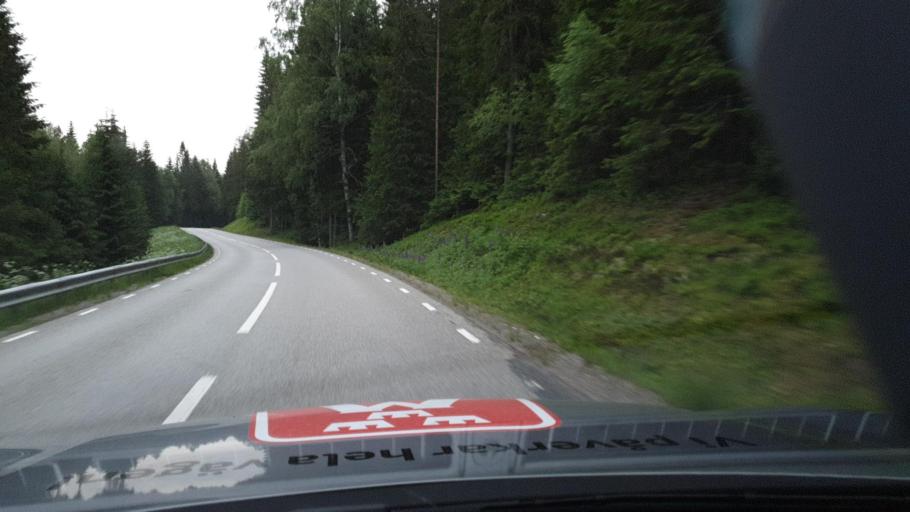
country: SE
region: OErebro
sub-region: Lindesbergs Kommun
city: Stora
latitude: 59.8959
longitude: 15.3086
